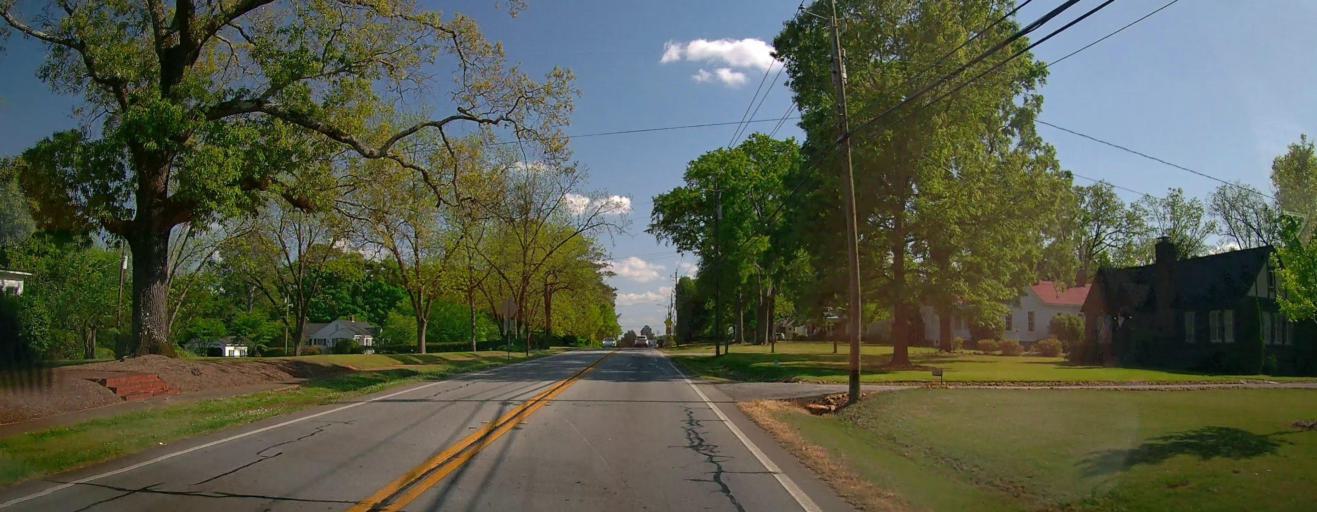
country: US
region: Georgia
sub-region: Morgan County
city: Madison
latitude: 33.5848
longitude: -83.4777
